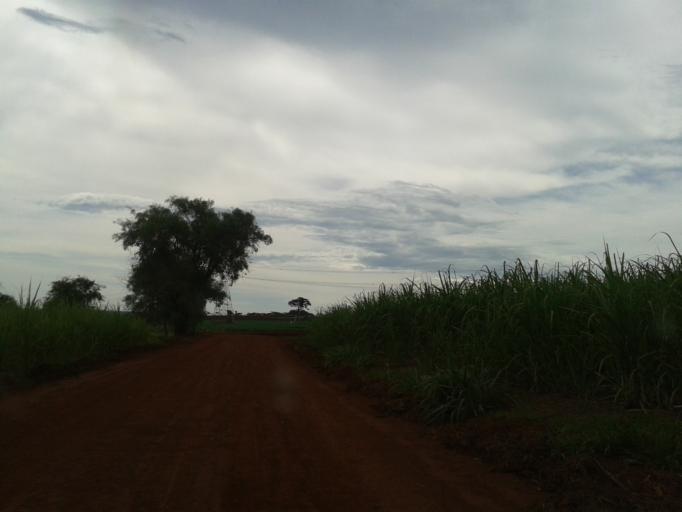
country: BR
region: Minas Gerais
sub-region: Centralina
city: Centralina
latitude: -18.6470
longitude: -49.3314
